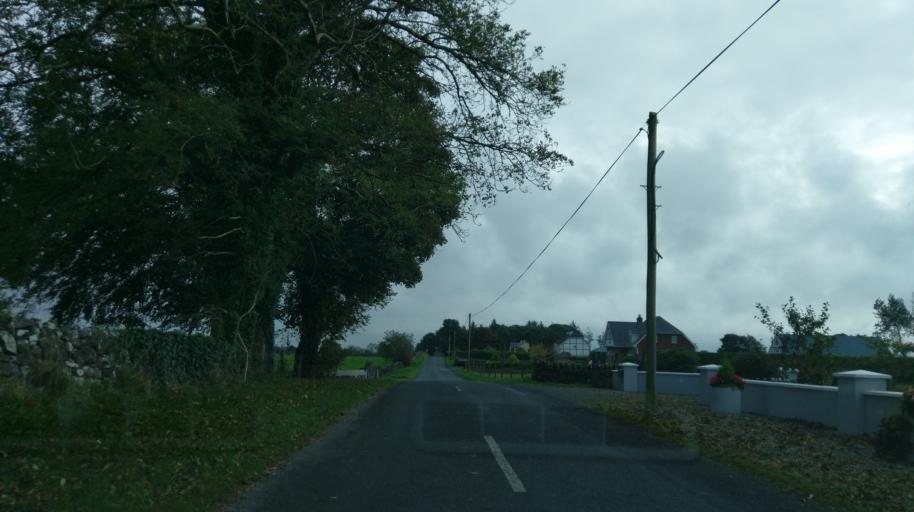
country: IE
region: Connaught
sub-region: County Galway
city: Athenry
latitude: 53.4571
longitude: -8.6070
